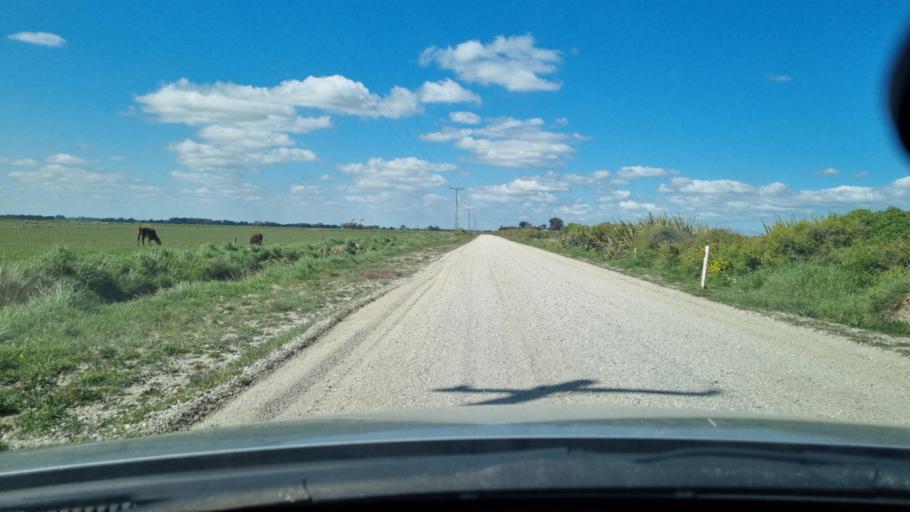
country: NZ
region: Southland
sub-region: Invercargill City
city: Invercargill
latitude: -46.3933
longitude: 168.2406
